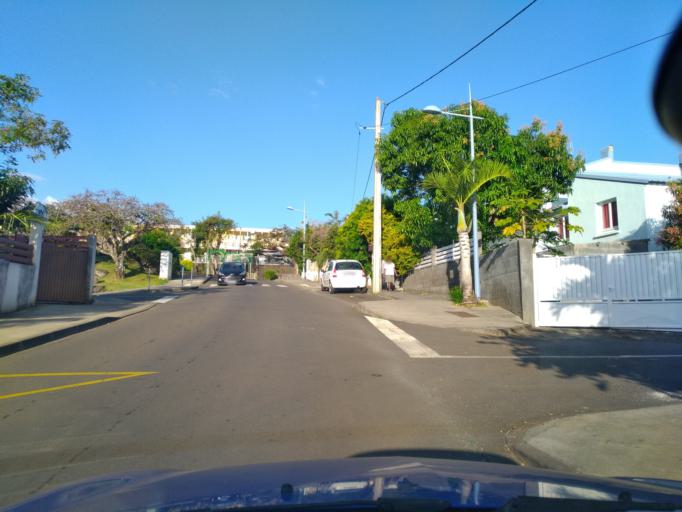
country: RE
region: Reunion
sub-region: Reunion
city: Saint-Pierre
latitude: -21.3425
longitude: 55.4850
